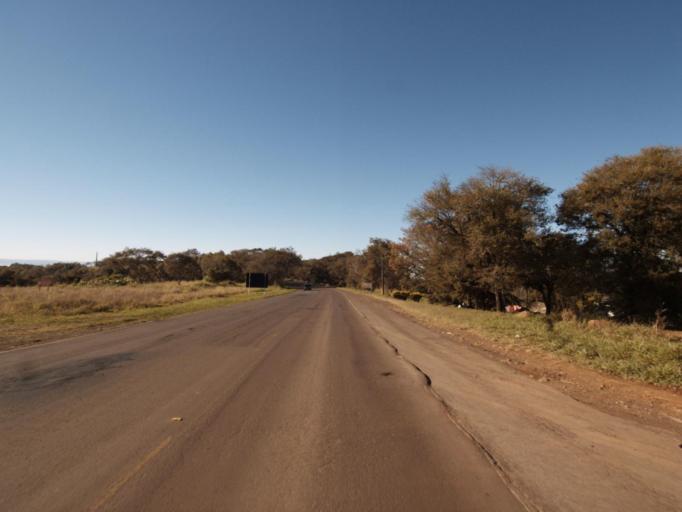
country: AR
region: Misiones
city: Bernardo de Irigoyen
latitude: -26.7648
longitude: -53.4956
